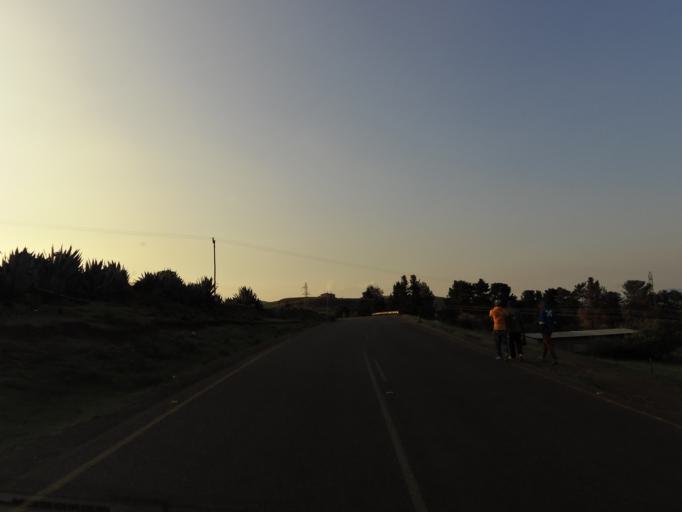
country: LS
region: Leribe
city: Leribe
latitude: -28.9980
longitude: 28.2049
